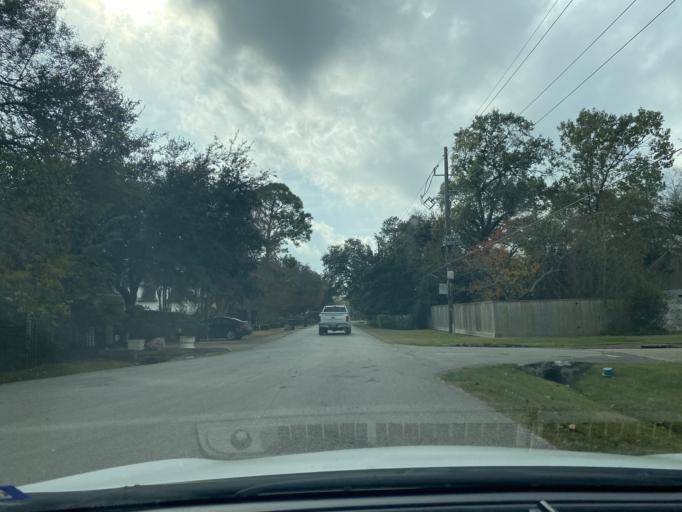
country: US
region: Texas
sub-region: Harris County
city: Hunters Creek Village
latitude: 29.7657
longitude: -95.4748
